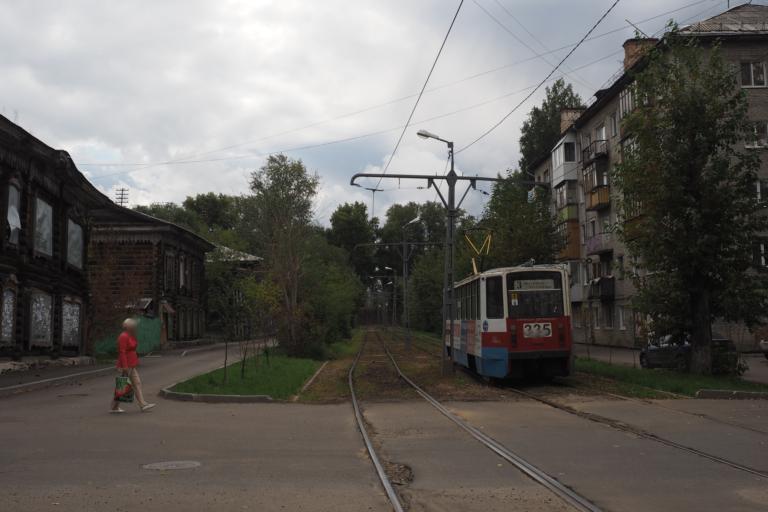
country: RU
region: Tomsk
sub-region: Tomskiy Rayon
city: Tomsk
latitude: 56.4830
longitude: 84.9532
